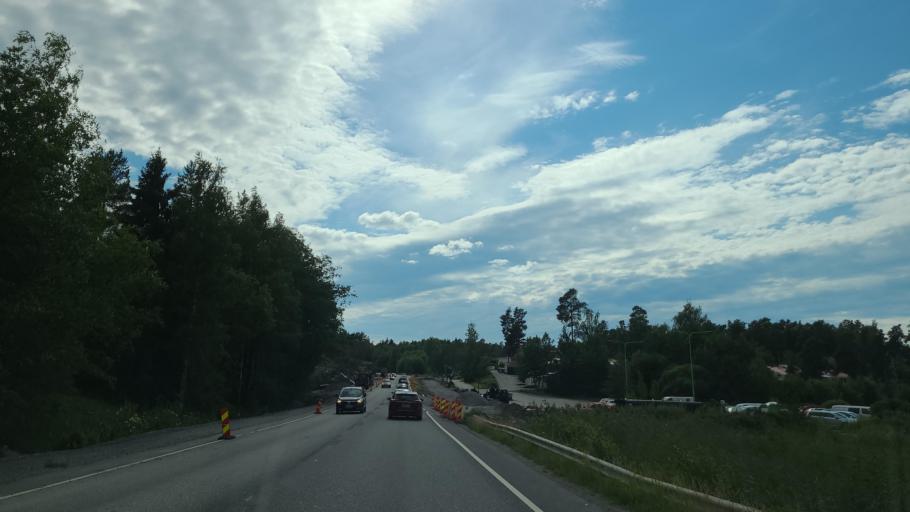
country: FI
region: Varsinais-Suomi
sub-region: Turku
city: Merimasku
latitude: 60.4602
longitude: 21.9177
